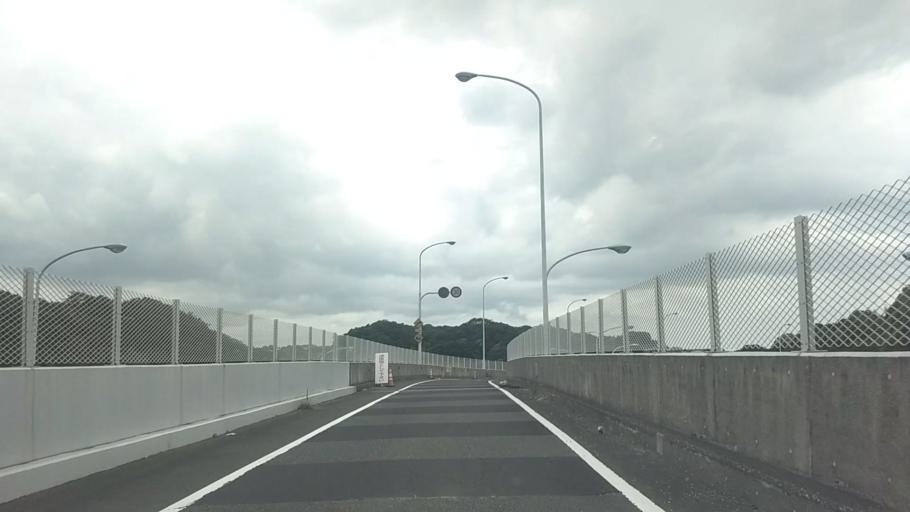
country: JP
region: Kanagawa
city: Fujisawa
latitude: 35.3605
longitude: 139.5090
